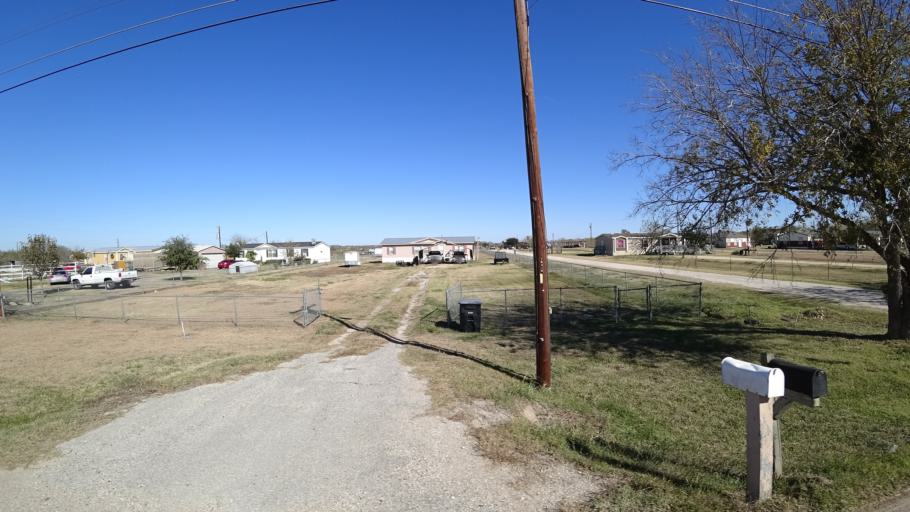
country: US
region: Texas
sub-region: Travis County
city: Garfield
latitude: 30.1220
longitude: -97.5967
